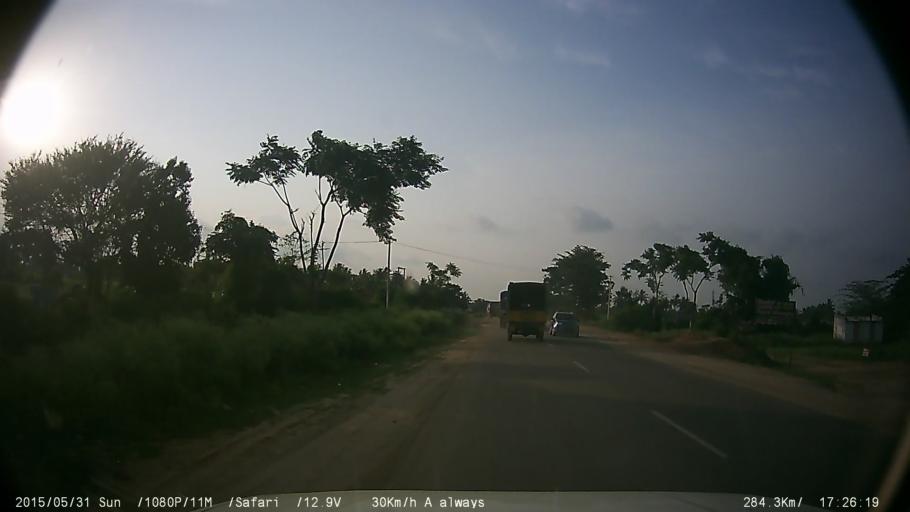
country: IN
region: Karnataka
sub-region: Chamrajnagar
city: Gundlupet
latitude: 11.8542
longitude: 76.6709
